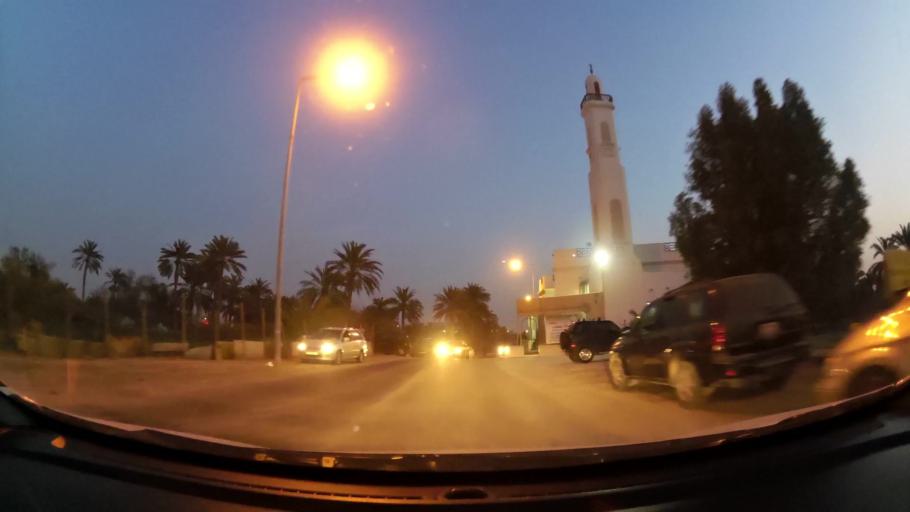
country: BH
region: Manama
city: Jidd Hafs
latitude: 26.2018
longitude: 50.5524
